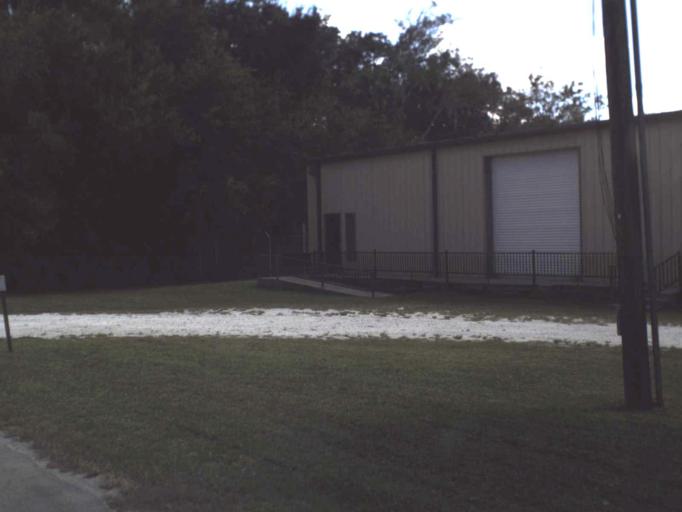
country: US
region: Florida
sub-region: Okeechobee County
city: Taylor Creek
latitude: 27.2096
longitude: -80.7911
